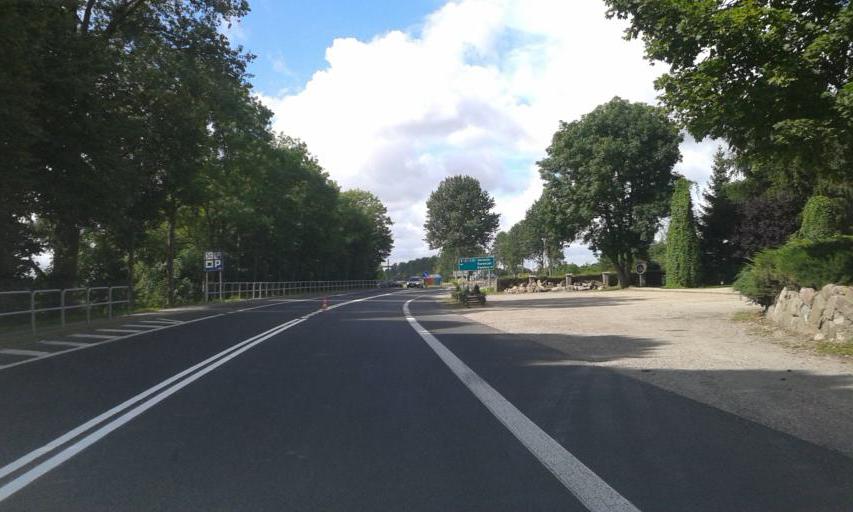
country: PL
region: West Pomeranian Voivodeship
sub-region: Powiat slawienski
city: Slawno
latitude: 54.3278
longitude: 16.5675
